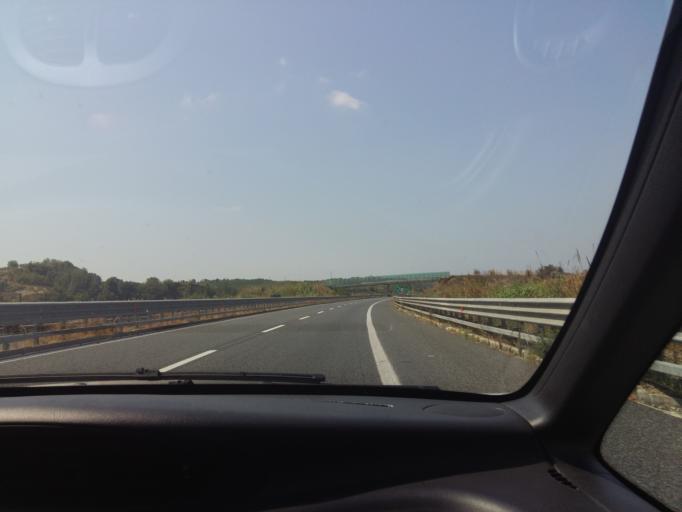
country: IT
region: Calabria
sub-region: Provincia di Reggio Calabria
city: Rosarno
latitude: 38.5012
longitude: 16.0302
